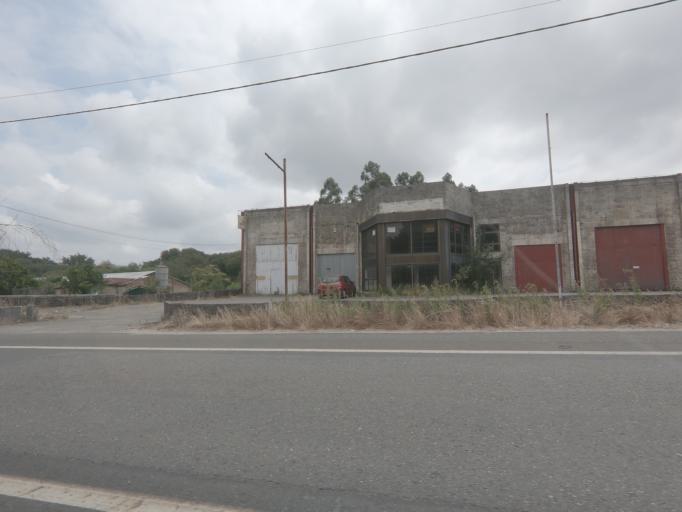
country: PT
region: Viana do Castelo
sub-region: Vila Nova de Cerveira
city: Vila Nova de Cerveira
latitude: 41.9502
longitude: -8.7700
